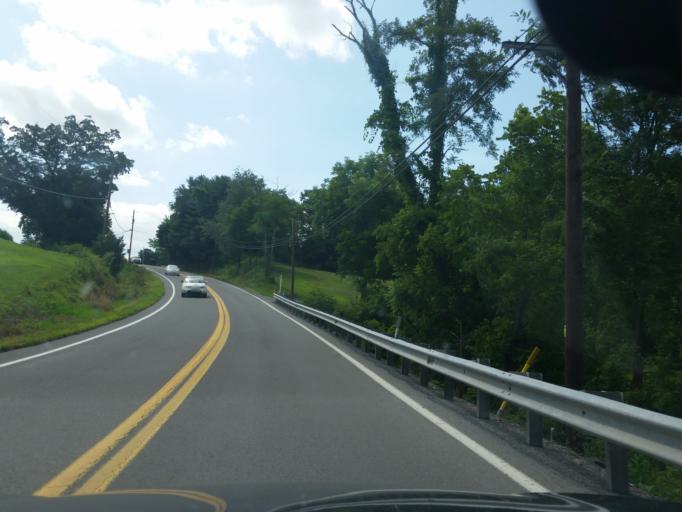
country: US
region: Pennsylvania
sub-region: Dauphin County
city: Elizabethville
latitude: 40.5147
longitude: -76.8597
